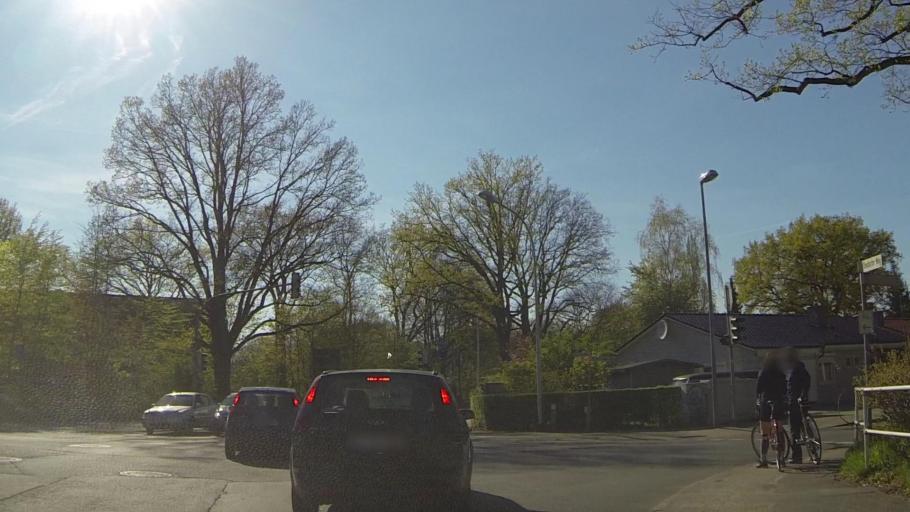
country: DE
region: Schleswig-Holstein
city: Rellingen
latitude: 53.6448
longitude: 9.7944
